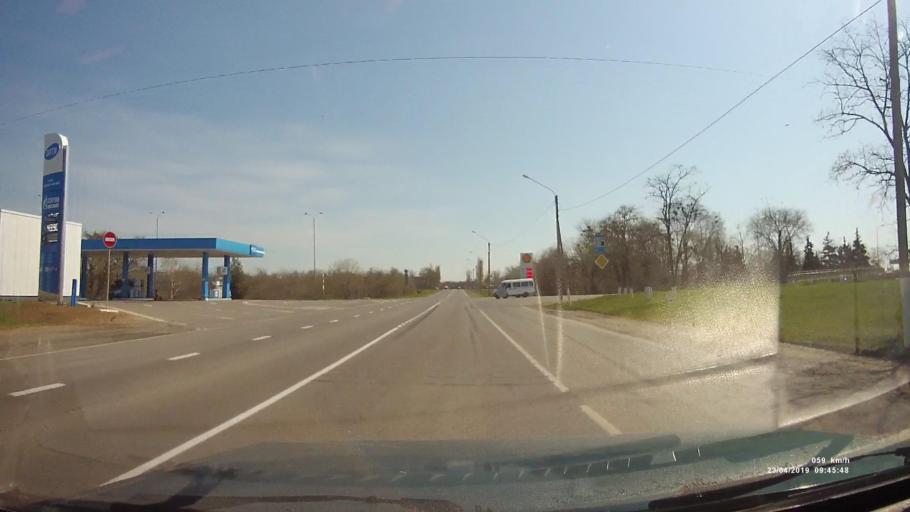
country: RU
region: Rostov
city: Orlovskiy
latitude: 46.8851
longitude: 42.0362
